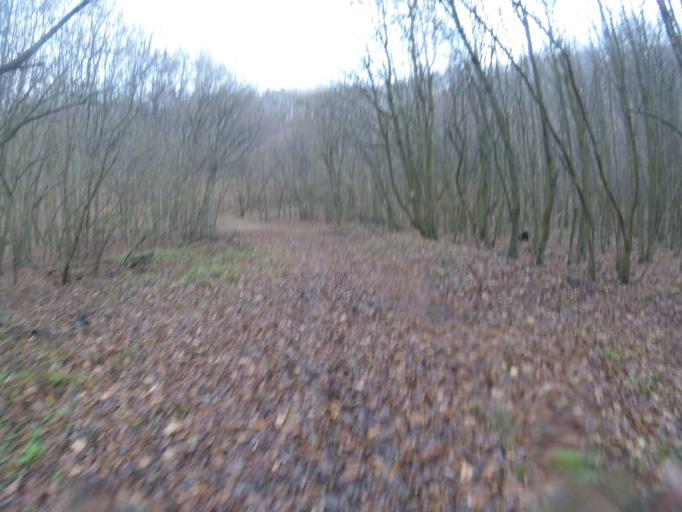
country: HU
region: Pest
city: Szob
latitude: 47.8653
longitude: 18.8488
